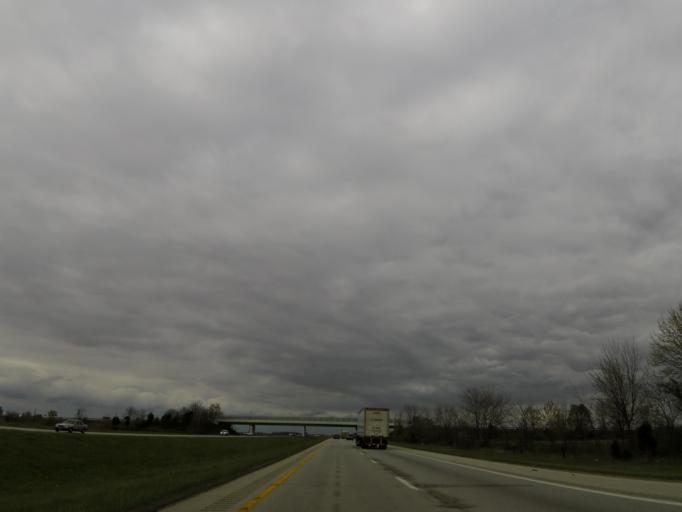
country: US
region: Ohio
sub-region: Clinton County
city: Wilmington
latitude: 39.5368
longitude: -83.7816
